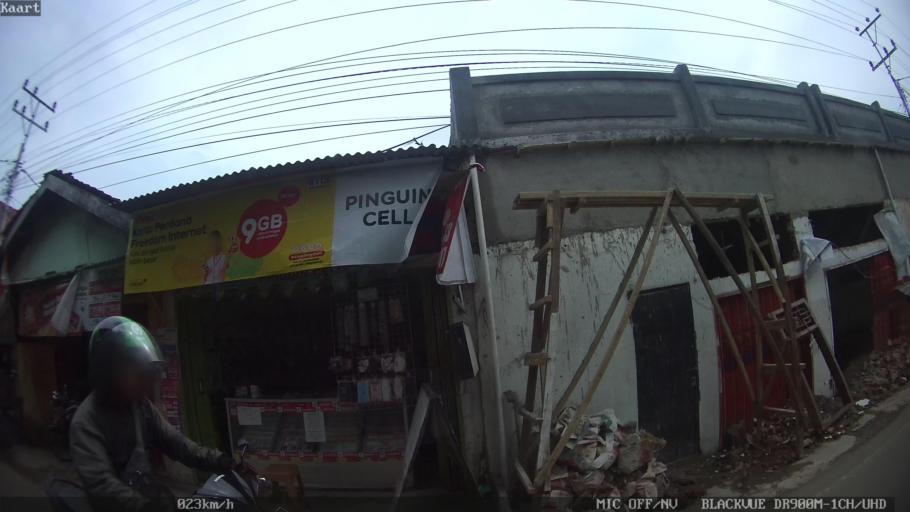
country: ID
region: Lampung
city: Kedaton
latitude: -5.3984
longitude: 105.2044
